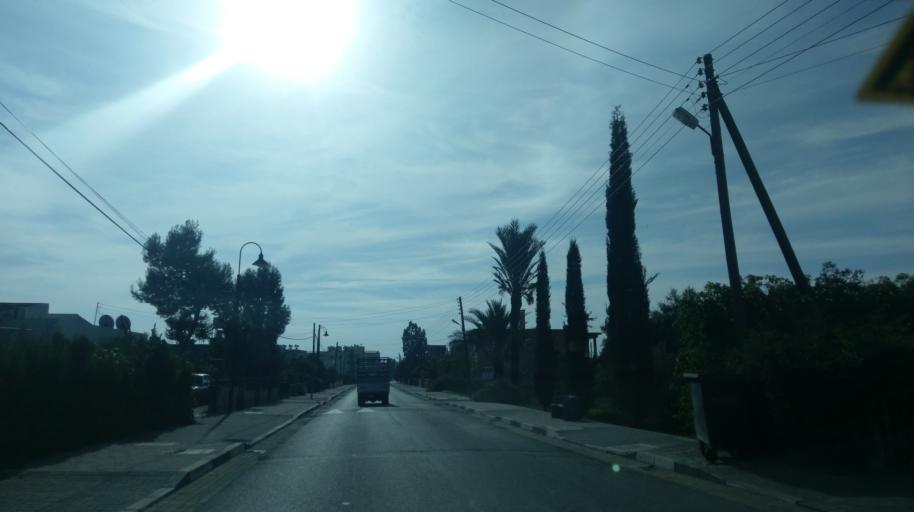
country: CY
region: Lefkosia
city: Geri
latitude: 35.2247
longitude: 33.5143
